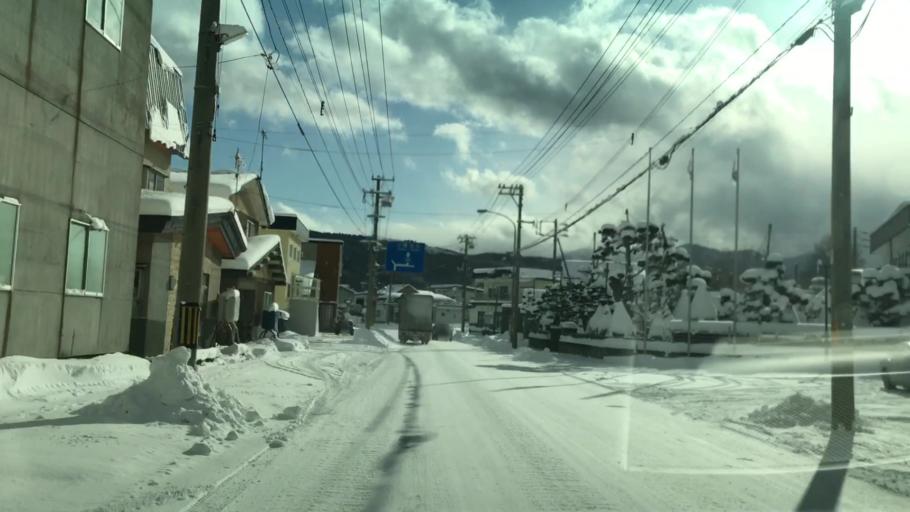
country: JP
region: Hokkaido
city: Yoichi
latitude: 43.2673
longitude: 140.6390
